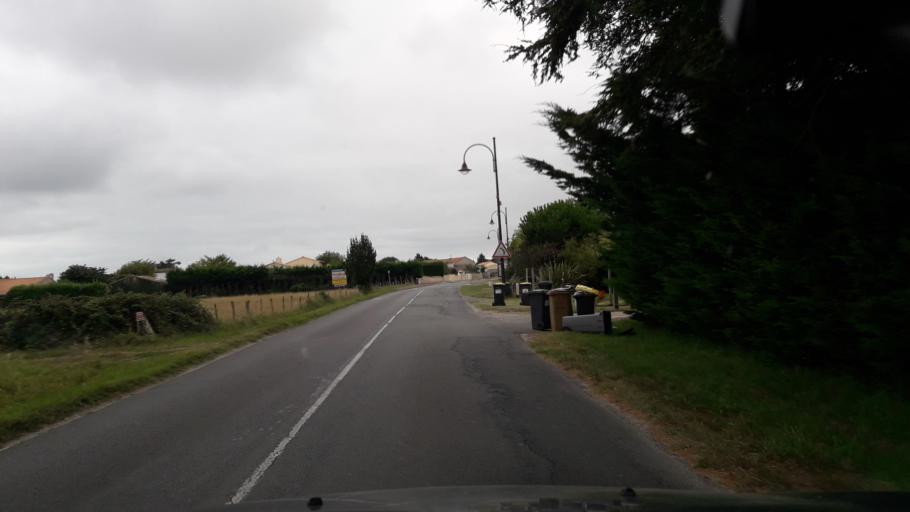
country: FR
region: Poitou-Charentes
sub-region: Departement de la Charente-Maritime
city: Les Mathes
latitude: 45.7258
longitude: -1.1413
